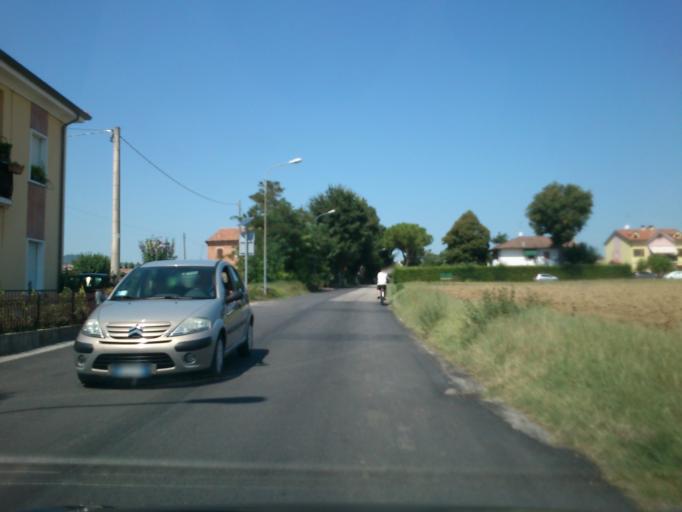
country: IT
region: The Marches
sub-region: Provincia di Pesaro e Urbino
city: Lucrezia
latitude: 43.7715
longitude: 12.9451
